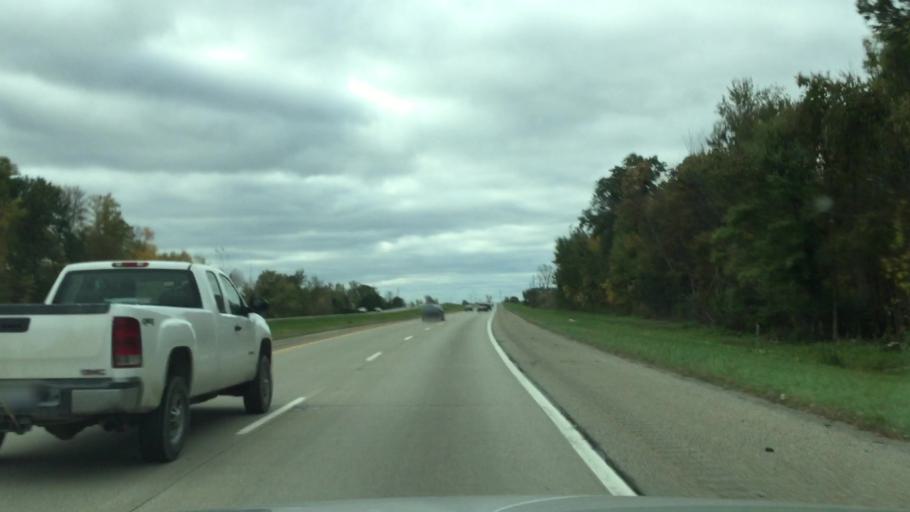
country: US
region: Michigan
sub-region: Macomb County
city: Romeo
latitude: 42.7931
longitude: -83.0022
